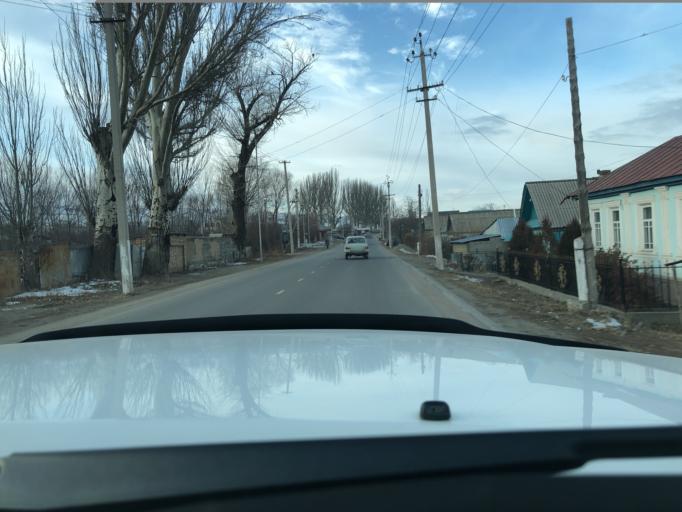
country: KG
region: Ysyk-Koel
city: Karakol
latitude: 42.4725
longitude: 78.3859
